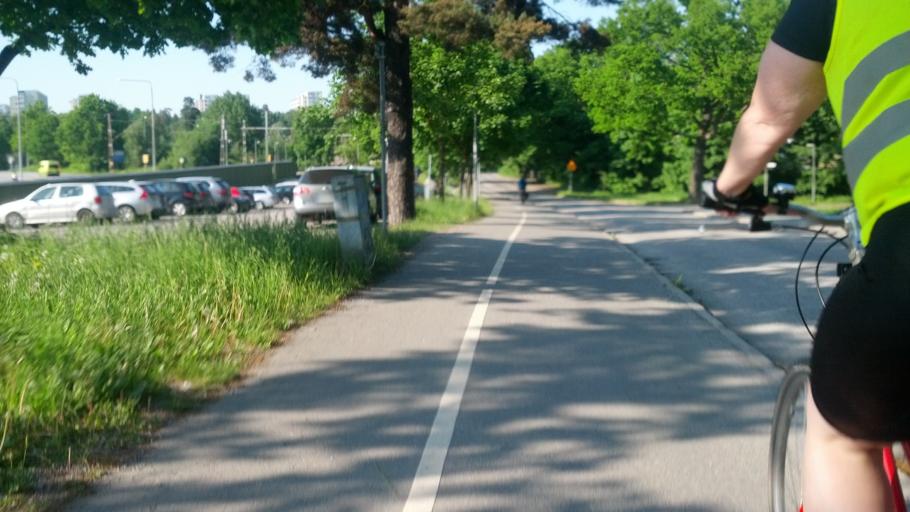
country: SE
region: Stockholm
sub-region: Danderyds Kommun
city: Djursholm
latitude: 59.3903
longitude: 18.0463
